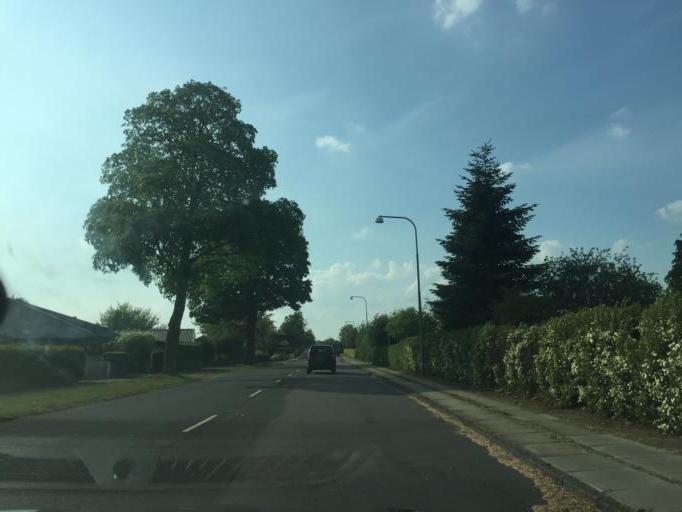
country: DK
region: South Denmark
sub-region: Odense Kommune
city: Bellinge
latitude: 55.3541
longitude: 10.3480
